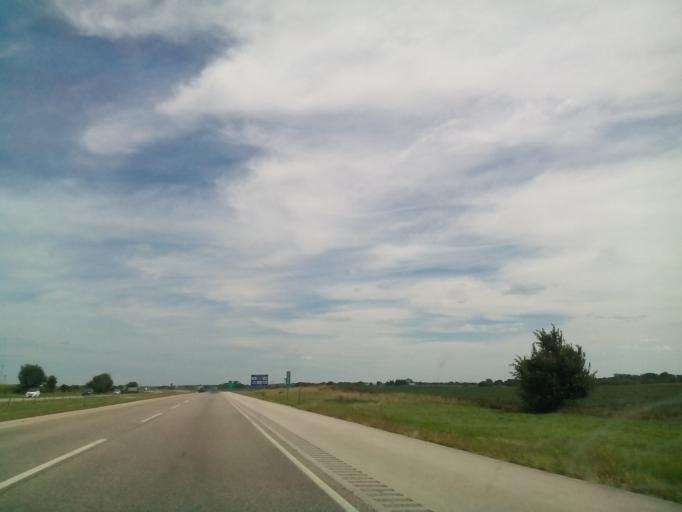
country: US
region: Illinois
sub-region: DeKalb County
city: DeKalb
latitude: 41.9001
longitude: -88.7976
